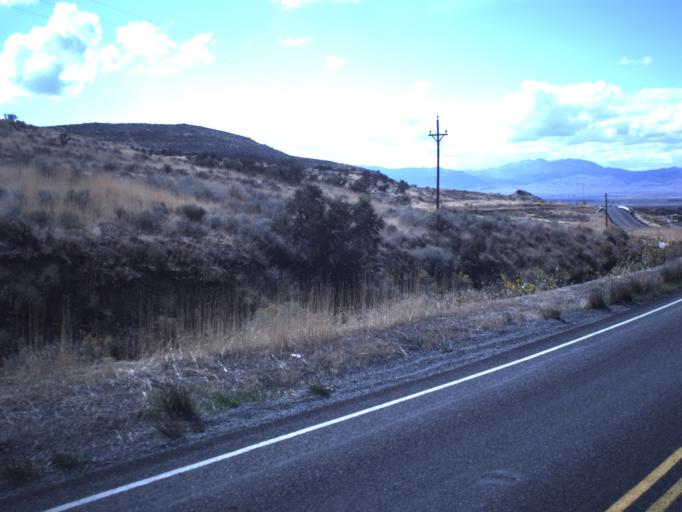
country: US
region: Utah
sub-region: Utah County
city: Genola
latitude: 40.0051
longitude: -111.8079
